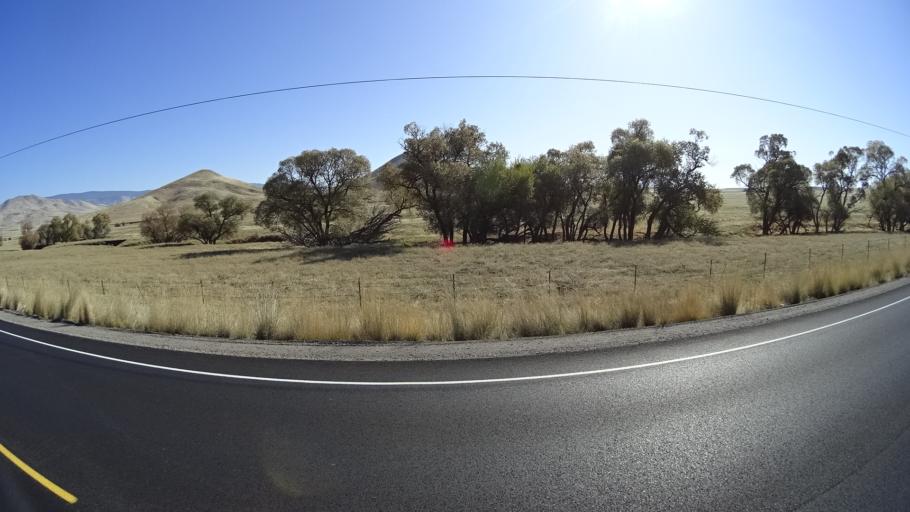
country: US
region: California
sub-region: Siskiyou County
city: Montague
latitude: 41.8291
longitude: -122.4927
